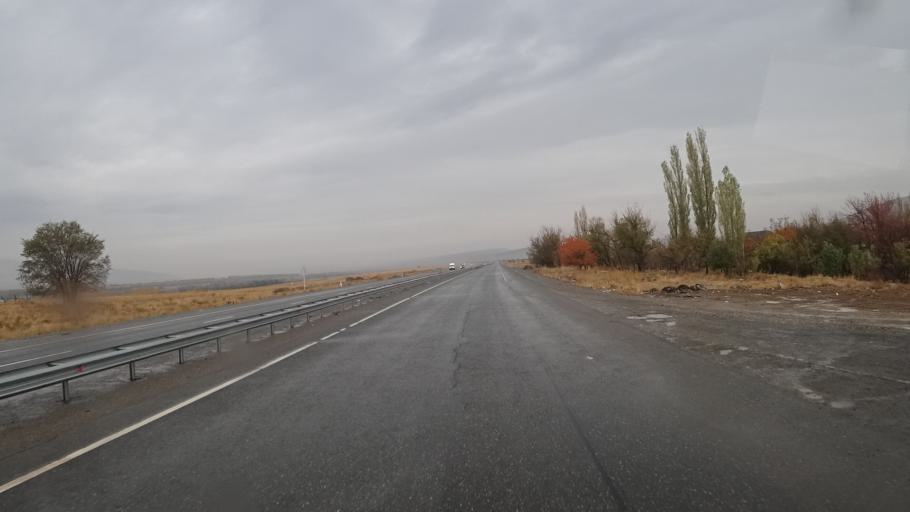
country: KZ
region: Ongtustik Qazaqstan
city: Turar Ryskulov
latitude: 42.5286
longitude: 70.3042
